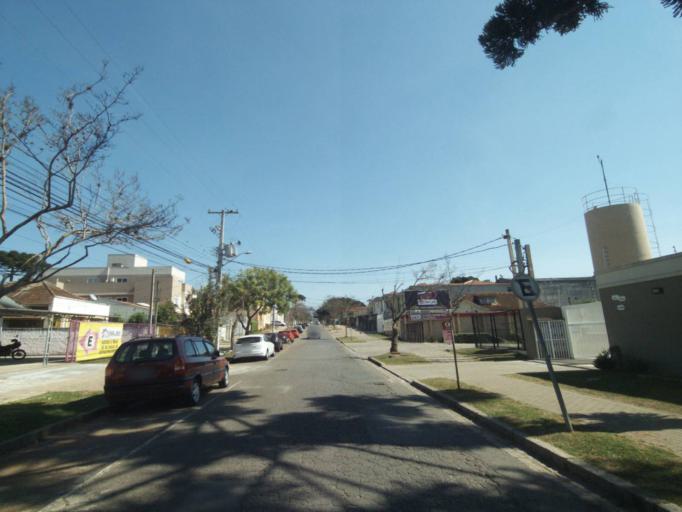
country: BR
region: Parana
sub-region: Curitiba
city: Curitiba
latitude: -25.4509
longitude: -49.2749
